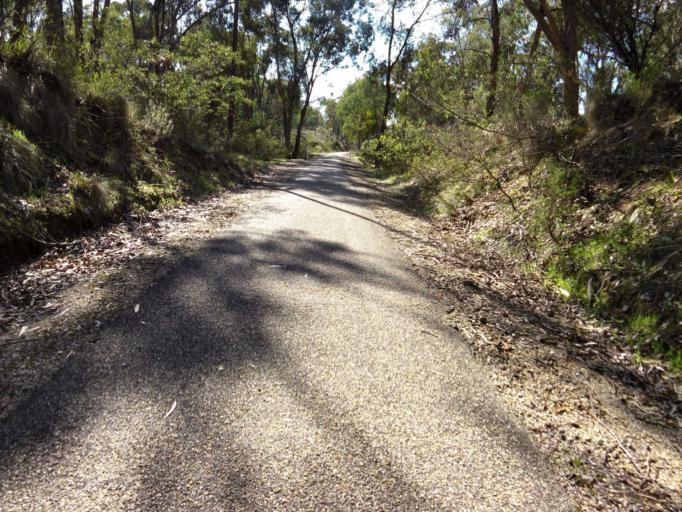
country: AU
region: Victoria
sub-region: Wangaratta
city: Wangaratta
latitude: -36.4074
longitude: 146.6180
